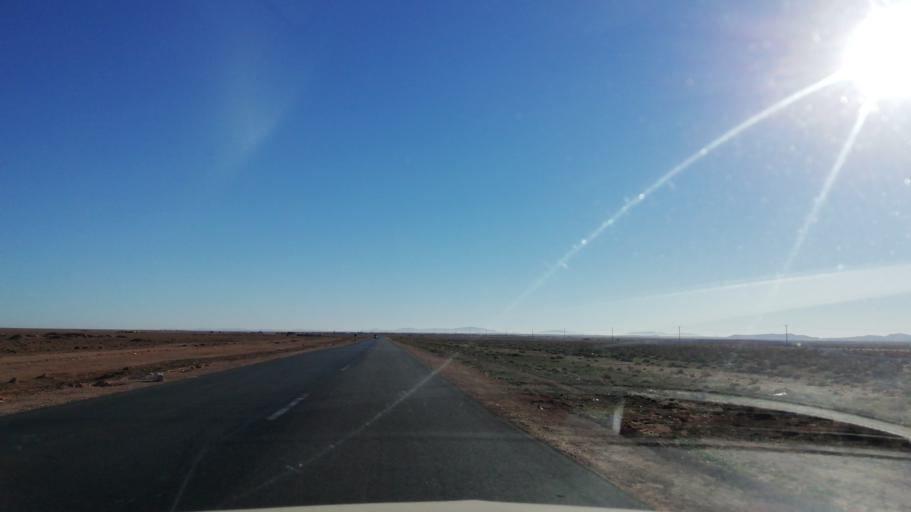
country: DZ
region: El Bayadh
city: El Bayadh
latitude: 33.8568
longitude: 0.5864
